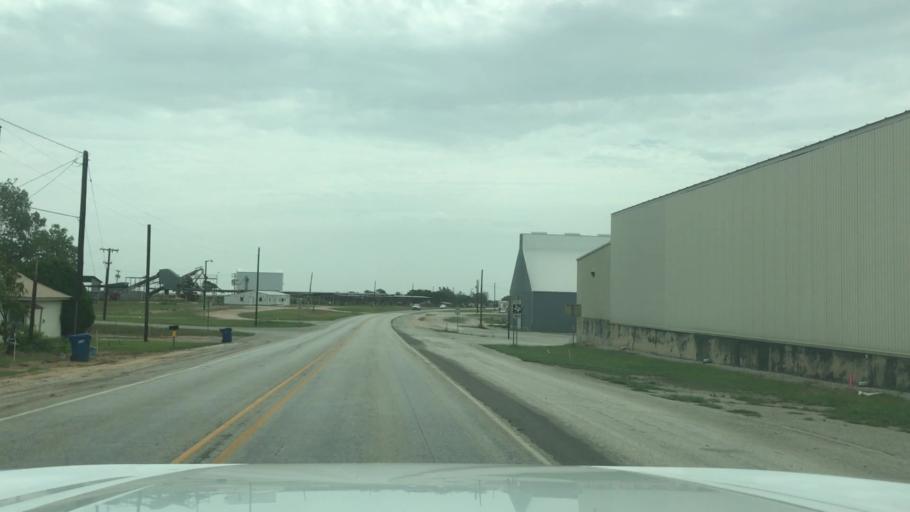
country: US
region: Texas
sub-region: Eastland County
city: Gorman
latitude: 32.2091
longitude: -98.6648
